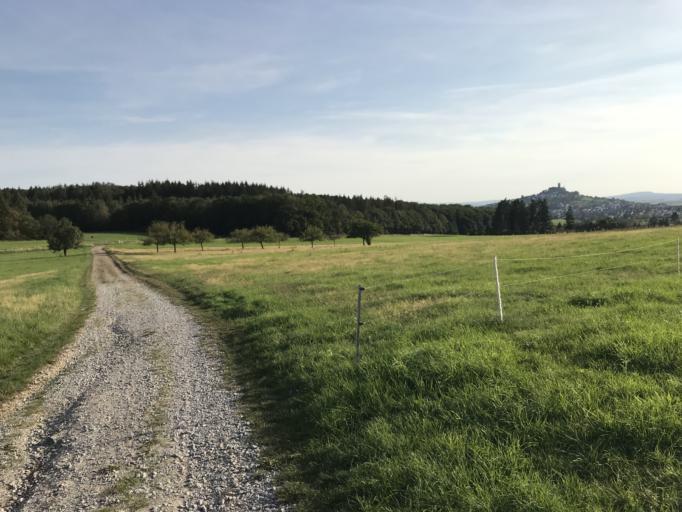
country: DE
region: Hesse
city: Lollar
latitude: 50.6372
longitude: 8.6548
